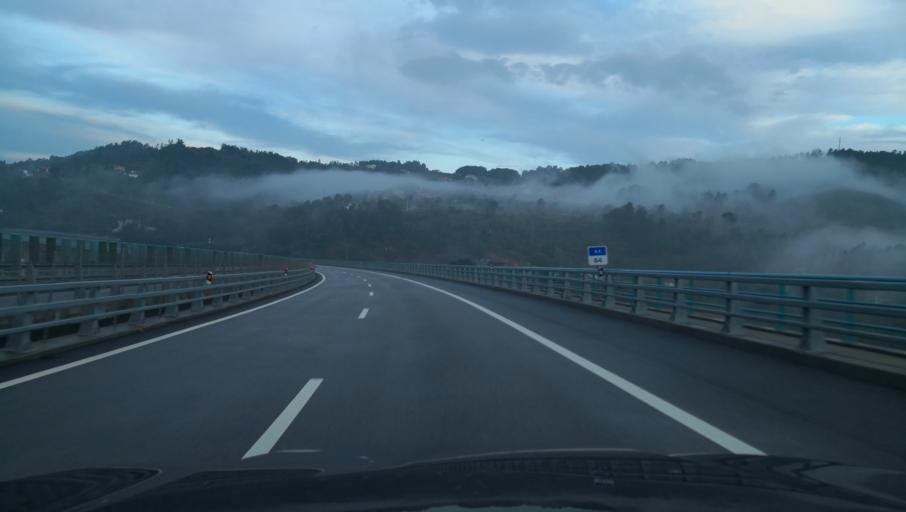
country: PT
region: Porto
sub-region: Amarante
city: Amarante
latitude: 41.2613
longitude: -8.0240
